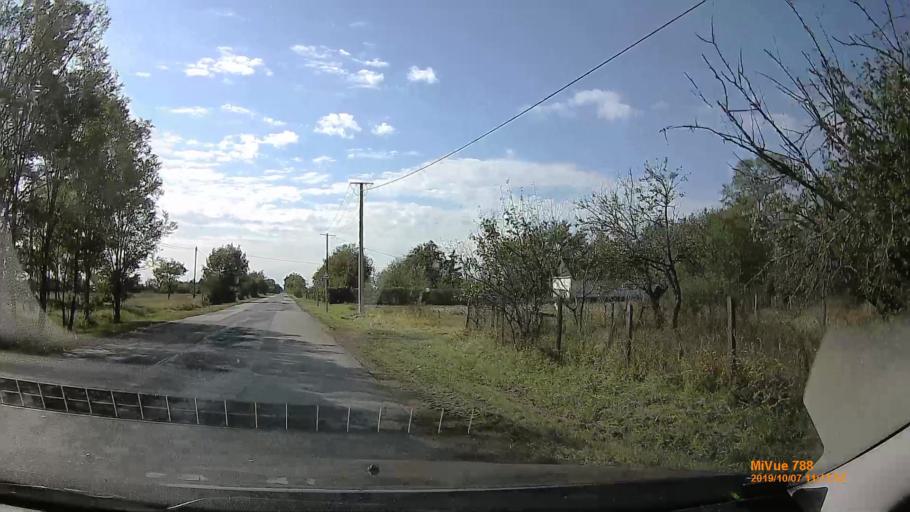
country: HU
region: Bekes
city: Kondoros
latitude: 46.7329
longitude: 20.7818
